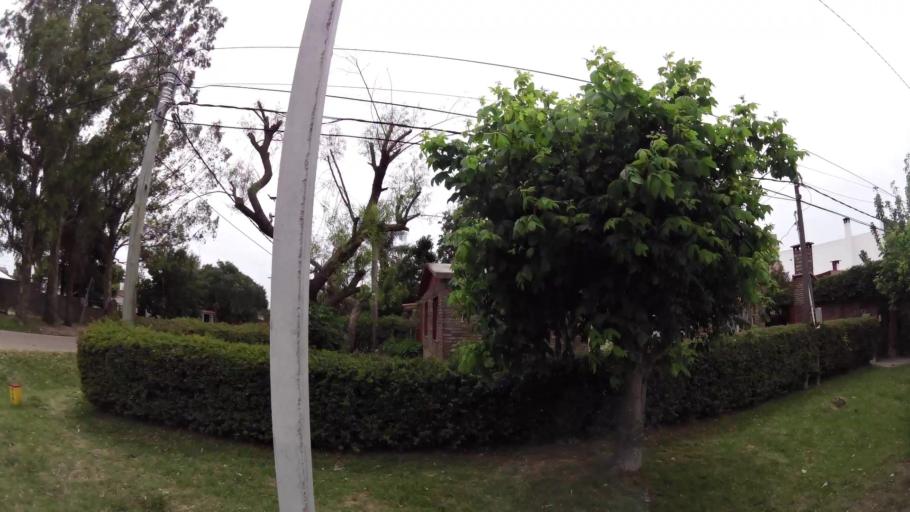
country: UY
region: Canelones
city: La Paz
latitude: -34.7560
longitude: -56.2258
